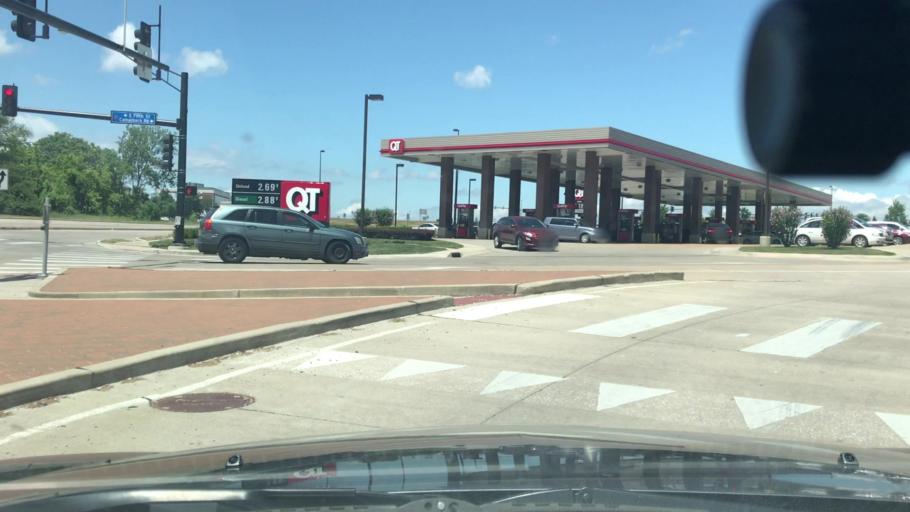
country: US
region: Missouri
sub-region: Saint Charles County
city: Saint Charles
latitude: 38.7648
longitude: -90.4958
